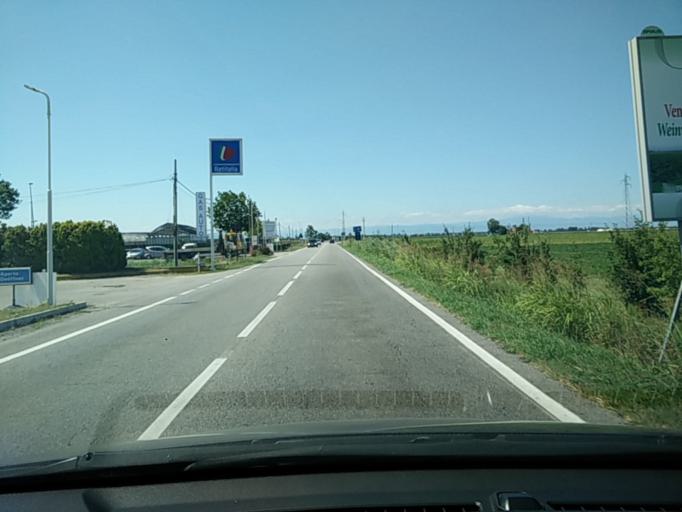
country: IT
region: Veneto
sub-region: Provincia di Venezia
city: La Salute di Livenza
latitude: 45.6530
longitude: 12.8334
